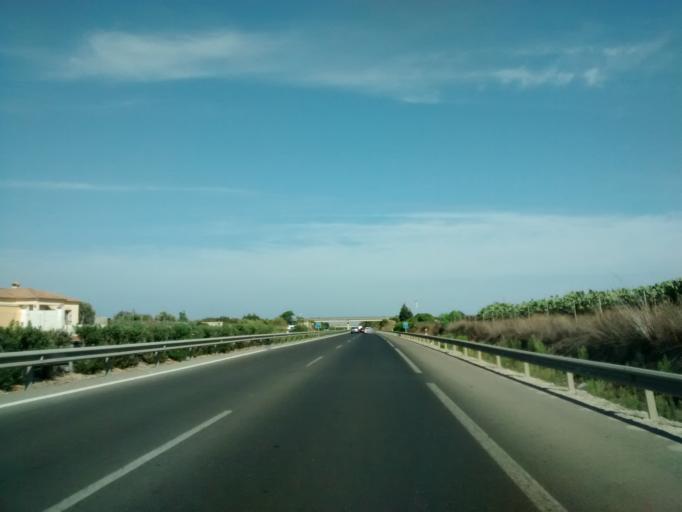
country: ES
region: Andalusia
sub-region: Provincia de Cadiz
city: Chiclana de la Frontera
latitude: 36.4311
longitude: -6.1173
